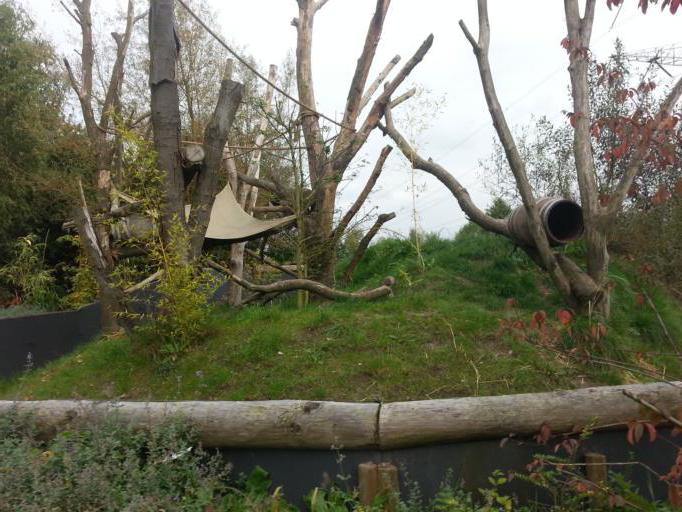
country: NL
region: North Brabant
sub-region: Gemeente Nuenen, Gerwen en Nederwetten
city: Nuenen
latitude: 51.4549
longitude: 5.5797
